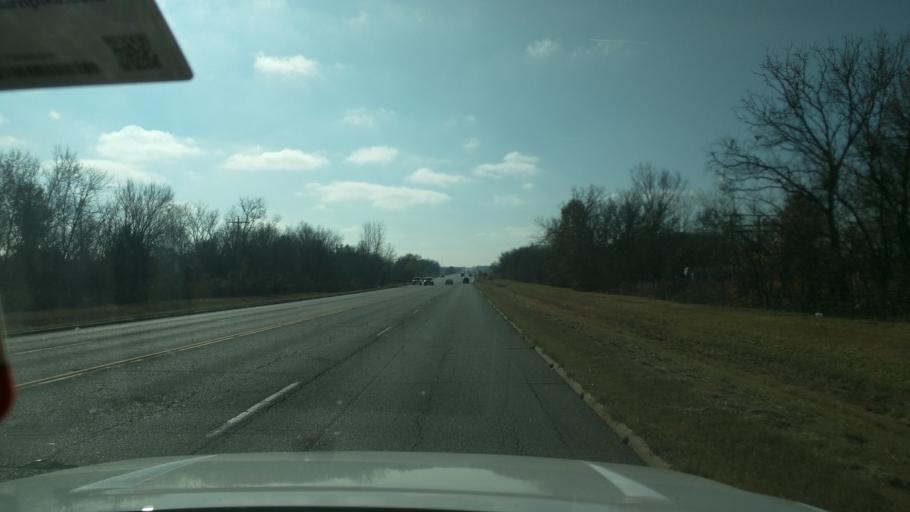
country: US
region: Oklahoma
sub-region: Washington County
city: Bartlesville
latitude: 36.6743
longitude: -95.9353
